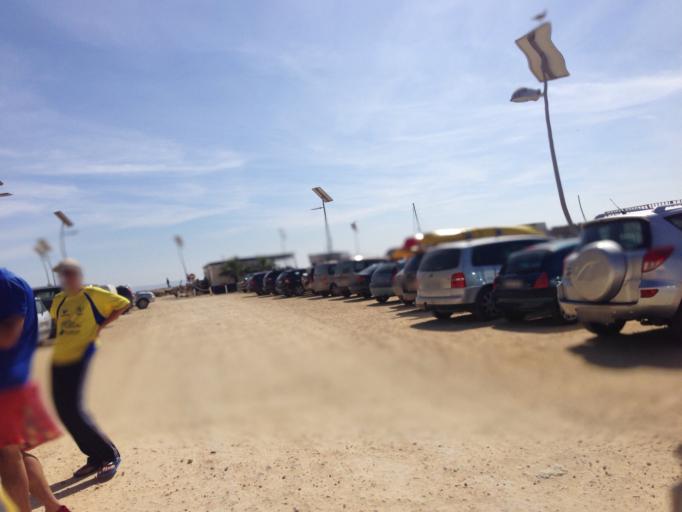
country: ES
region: Andalusia
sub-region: Provincia de Cadiz
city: Conil de la Frontera
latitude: 36.2957
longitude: -6.1363
